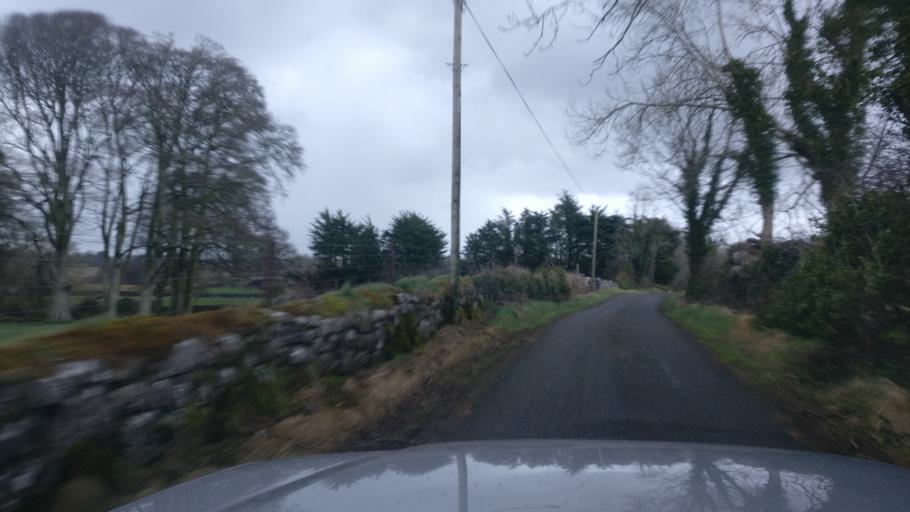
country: IE
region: Connaught
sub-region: County Galway
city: Loughrea
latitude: 53.1851
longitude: -8.6668
